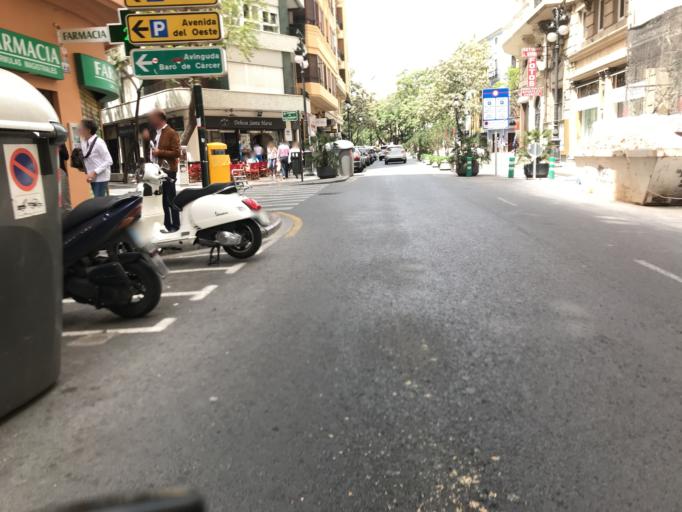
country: ES
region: Valencia
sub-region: Provincia de Valencia
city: Valencia
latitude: 39.4725
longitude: -0.3771
